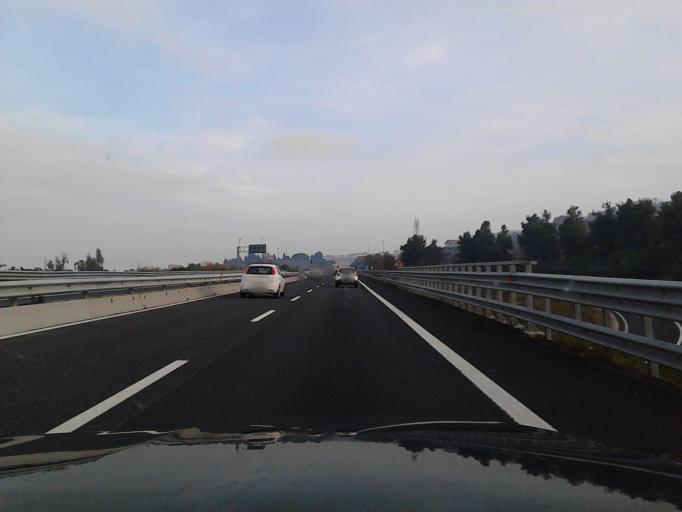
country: IT
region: Abruzzo
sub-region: Provincia di Teramo
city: Borgo Santa Maria Immacolata
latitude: 42.6068
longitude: 14.0466
